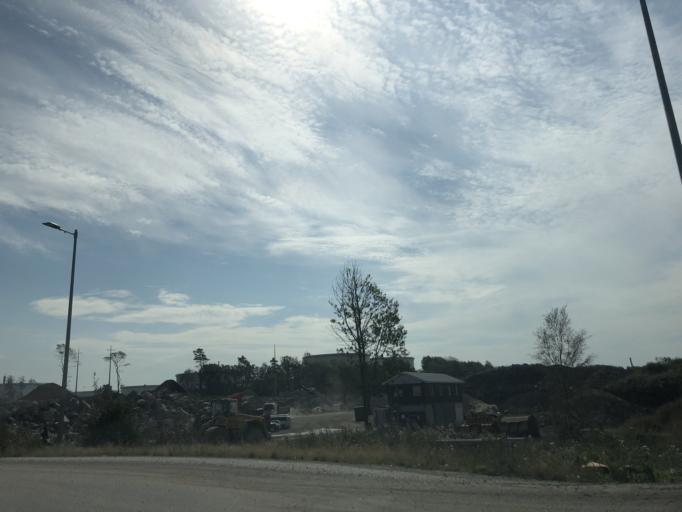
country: SE
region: Vaestra Goetaland
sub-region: Goteborg
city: Majorna
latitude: 57.7070
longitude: 11.8681
